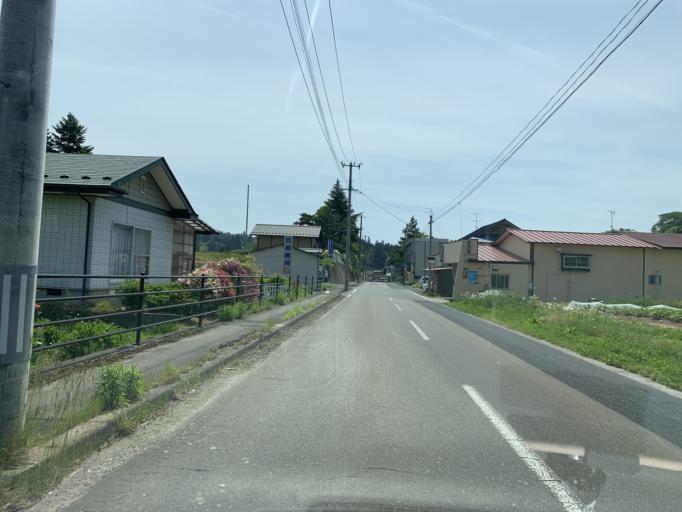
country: JP
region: Iwate
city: Ichinoseki
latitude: 38.9763
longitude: 141.2049
